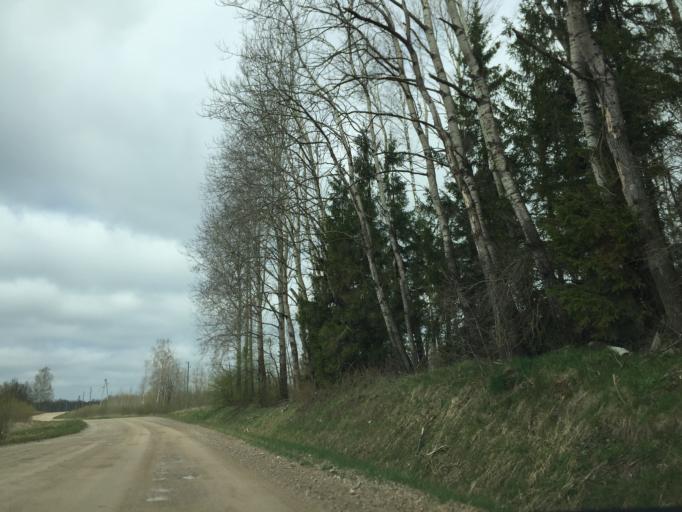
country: EE
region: Valgamaa
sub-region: Valga linn
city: Valga
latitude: 57.5636
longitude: 26.2719
